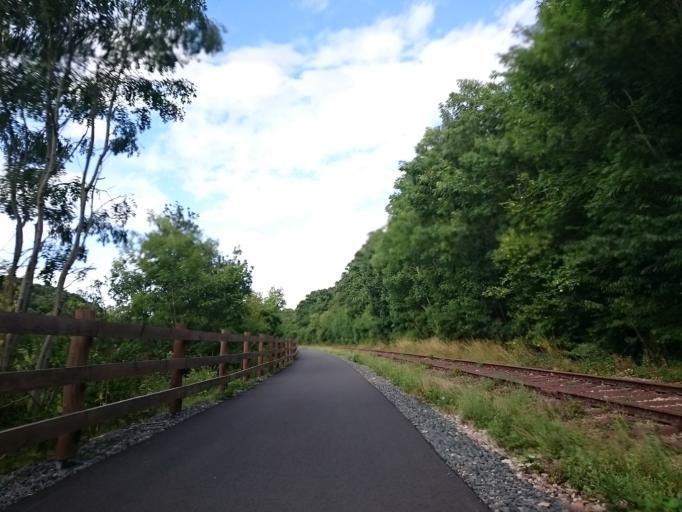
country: FR
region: Lower Normandy
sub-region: Departement du Calvados
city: Clinchamps-sur-Orne
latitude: 49.0681
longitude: -0.4359
